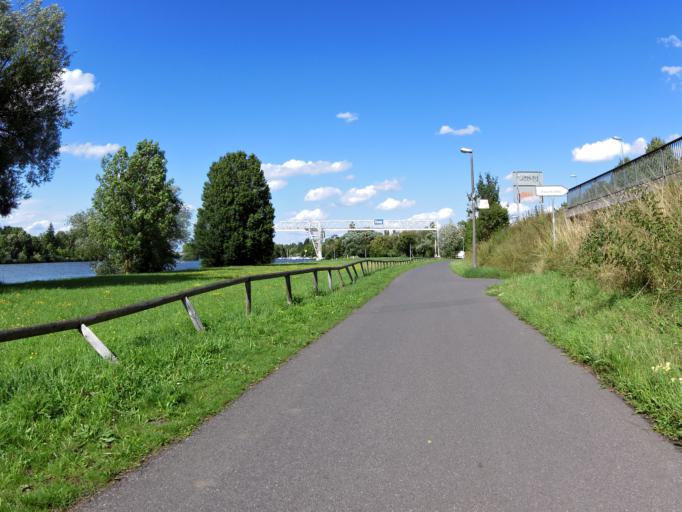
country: DE
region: Bavaria
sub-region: Regierungsbezirk Unterfranken
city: Kitzingen
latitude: 49.7265
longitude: 10.1655
